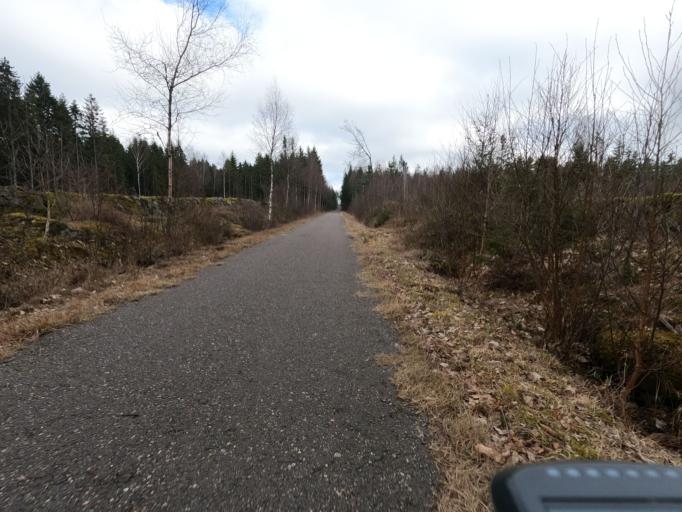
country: SE
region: Joenkoeping
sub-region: Varnamo Kommun
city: Rydaholm
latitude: 56.8460
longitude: 14.2157
